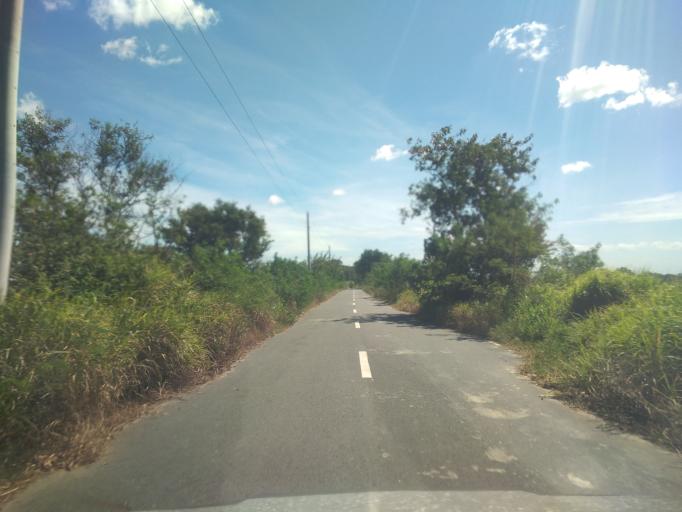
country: PH
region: Central Luzon
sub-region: Province of Pampanga
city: Balas
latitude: 15.0502
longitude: 120.5864
